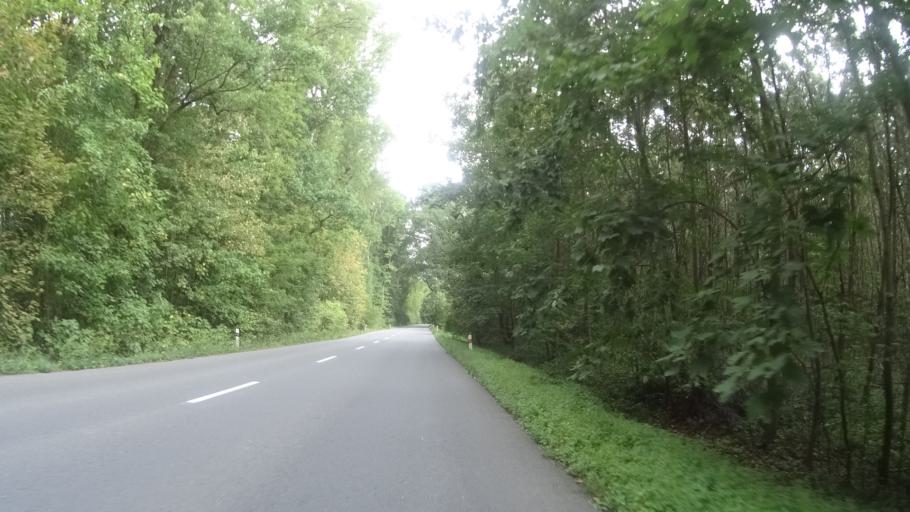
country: CZ
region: Zlin
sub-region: Okres Kromeriz
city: Kromeriz
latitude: 49.3298
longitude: 17.3861
